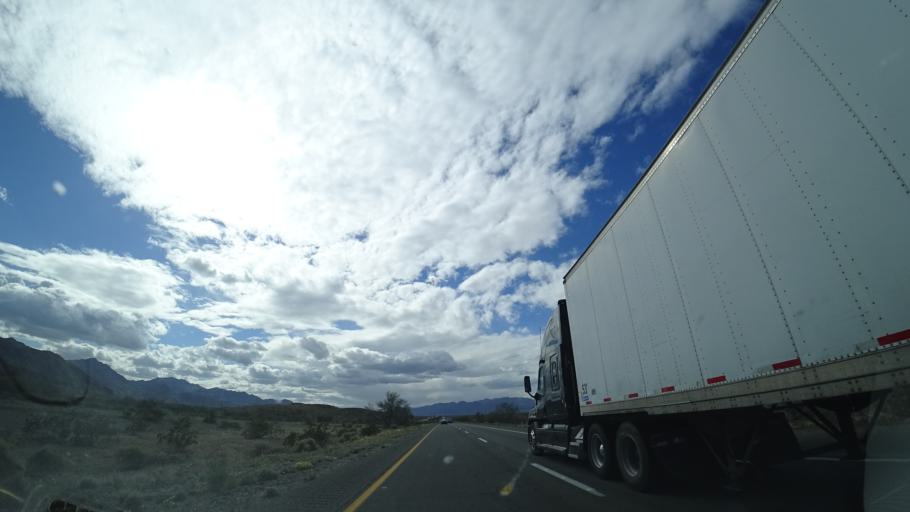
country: US
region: California
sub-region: Imperial County
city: Niland
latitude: 33.7059
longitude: -115.3411
